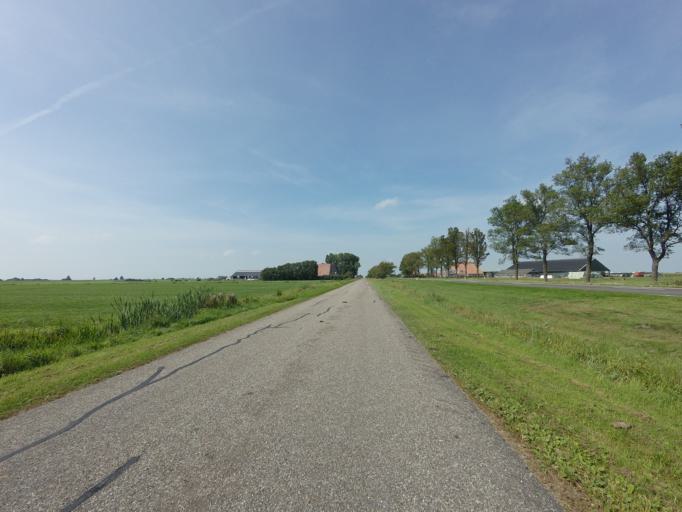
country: NL
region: Friesland
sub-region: Sudwest Fryslan
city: Woudsend
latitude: 52.9243
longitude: 5.6779
